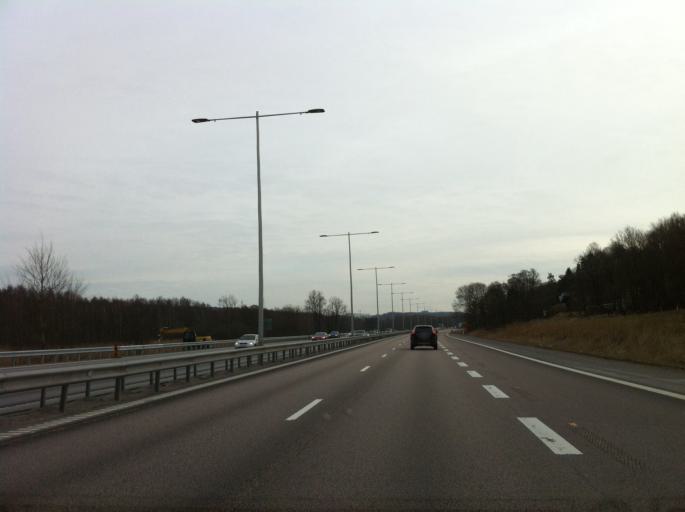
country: SE
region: Vaestra Goetaland
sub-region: Kungalvs Kommun
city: Kungalv
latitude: 57.8897
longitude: 11.9383
